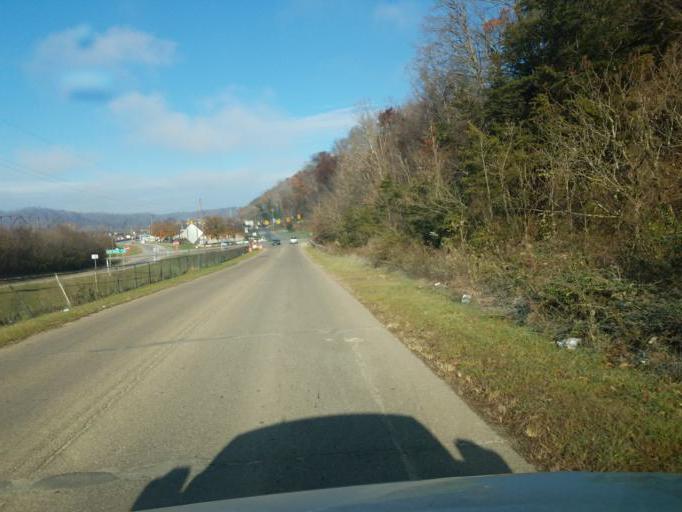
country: US
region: Ohio
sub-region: Scioto County
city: Sciotodale
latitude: 38.7506
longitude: -82.8750
